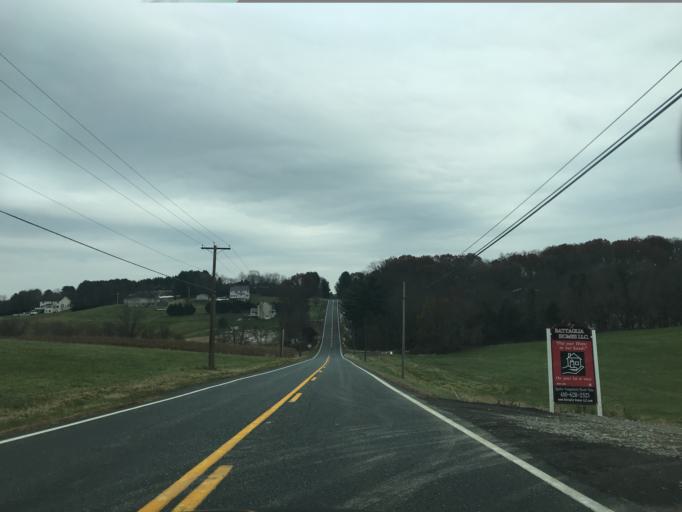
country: US
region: Pennsylvania
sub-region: York County
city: Susquehanna Trails
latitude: 39.6792
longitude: -76.3689
